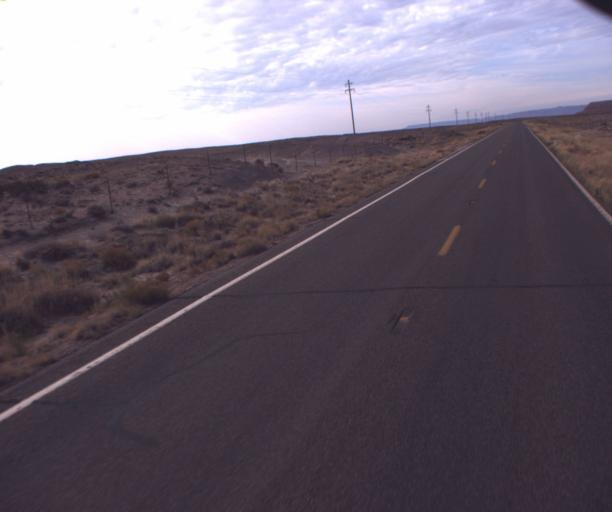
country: US
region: Arizona
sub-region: Apache County
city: Many Farms
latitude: 36.4750
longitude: -109.5170
